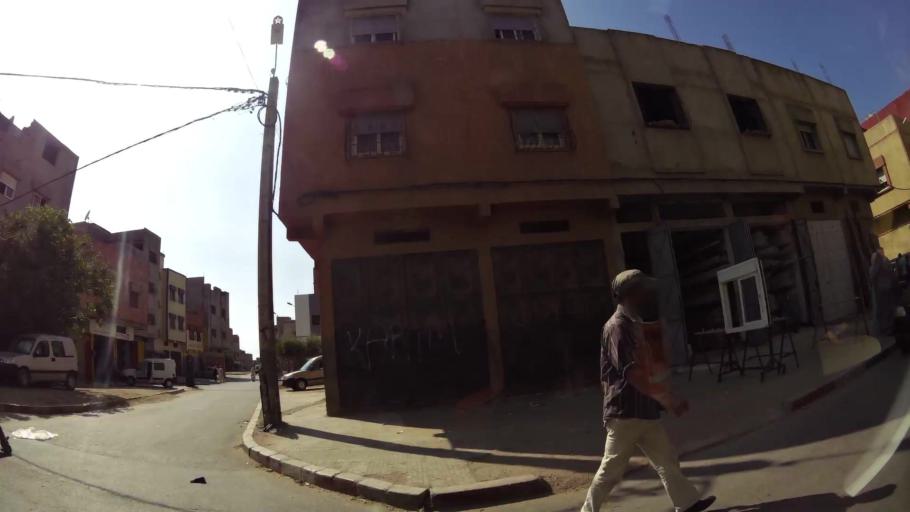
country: MA
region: Rabat-Sale-Zemmour-Zaer
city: Sale
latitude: 34.0685
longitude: -6.7693
